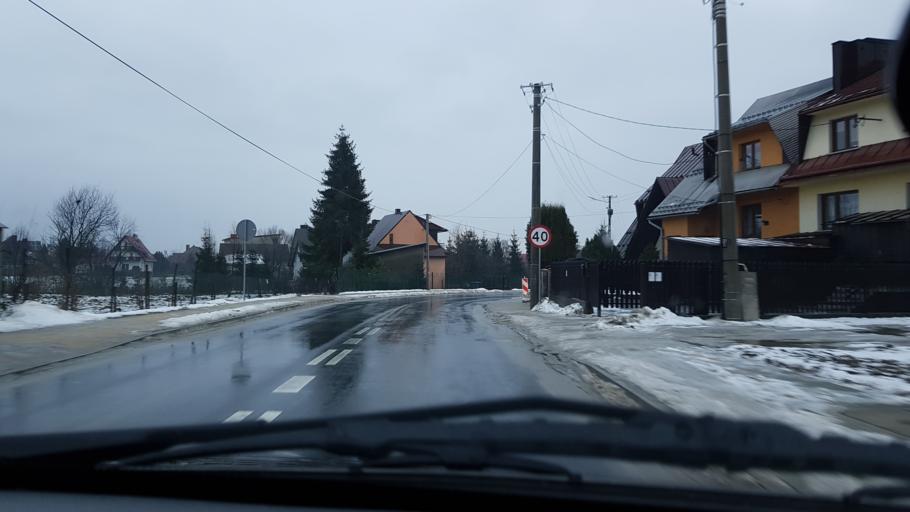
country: PL
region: Lesser Poland Voivodeship
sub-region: Powiat nowotarski
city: Ludzmierz
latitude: 49.4848
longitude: 20.0014
